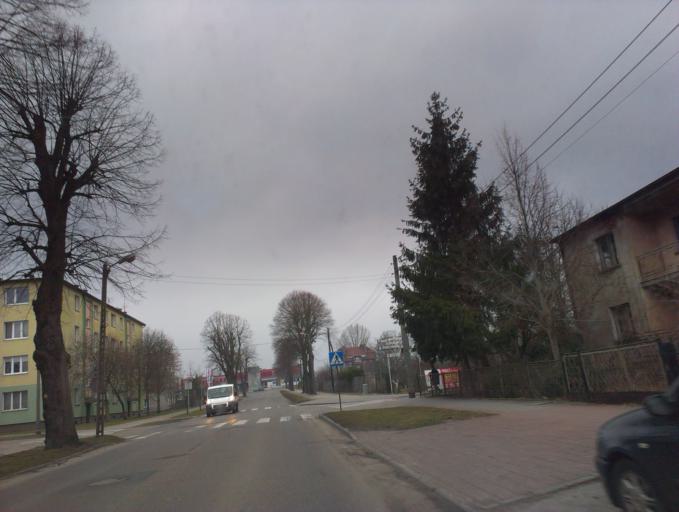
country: PL
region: Greater Poland Voivodeship
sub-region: Powiat chodzieski
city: Chodziez
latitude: 52.9945
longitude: 16.9137
